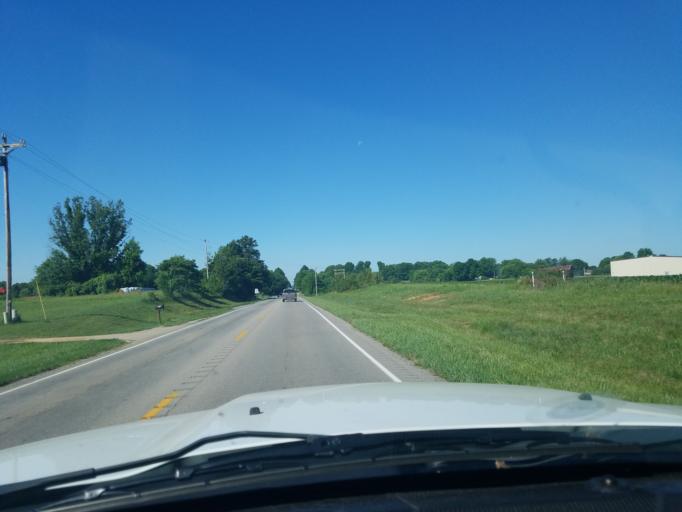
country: US
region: Kentucky
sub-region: Barren County
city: Glasgow
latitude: 36.9509
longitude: -85.9664
